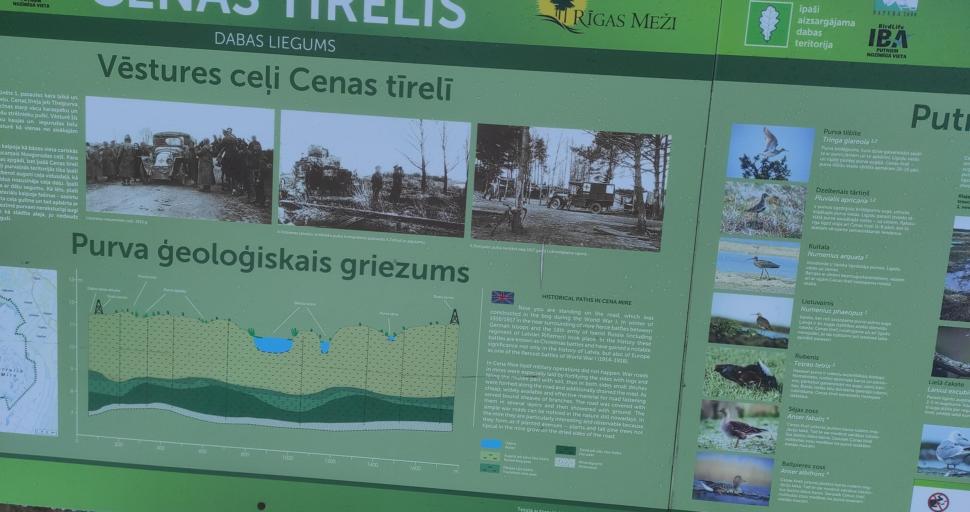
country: LV
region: Babite
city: Pinki
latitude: 56.8526
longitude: 23.8255
